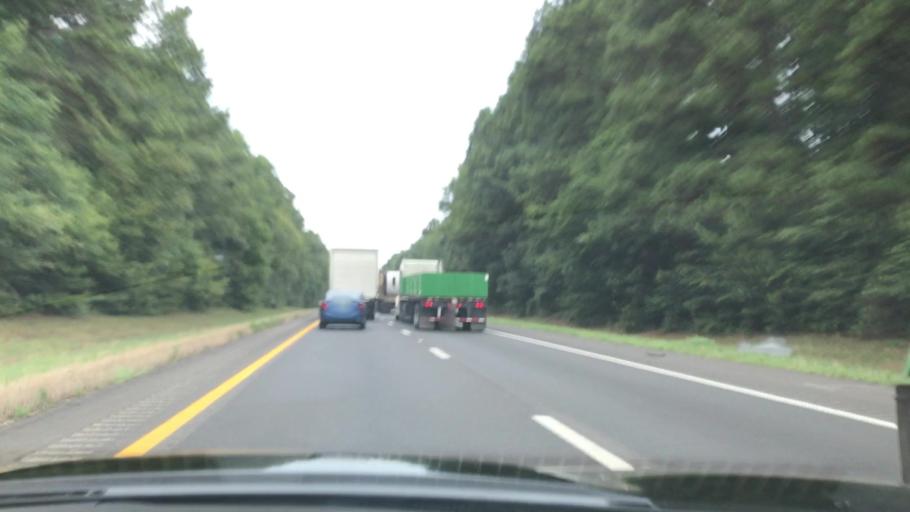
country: US
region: Texas
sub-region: Harrison County
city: Marshall
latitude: 32.4879
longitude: -94.4464
